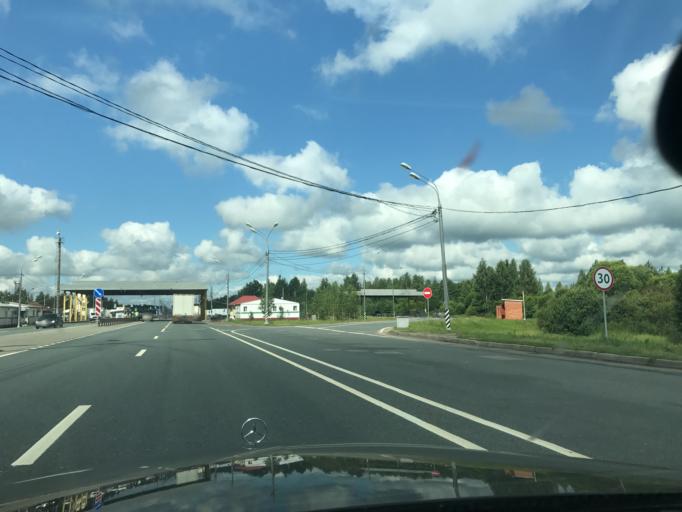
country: RU
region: Smolensk
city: Rudnya
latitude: 54.6912
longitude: 31.0188
